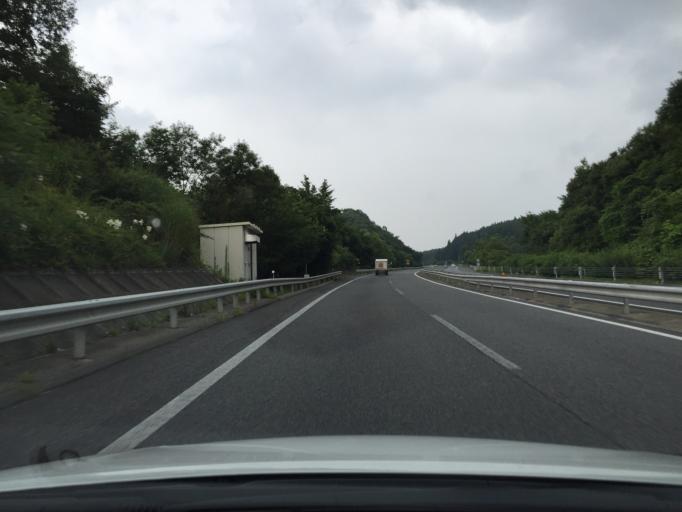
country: JP
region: Fukushima
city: Funehikimachi-funehiki
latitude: 37.2294
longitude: 140.6828
